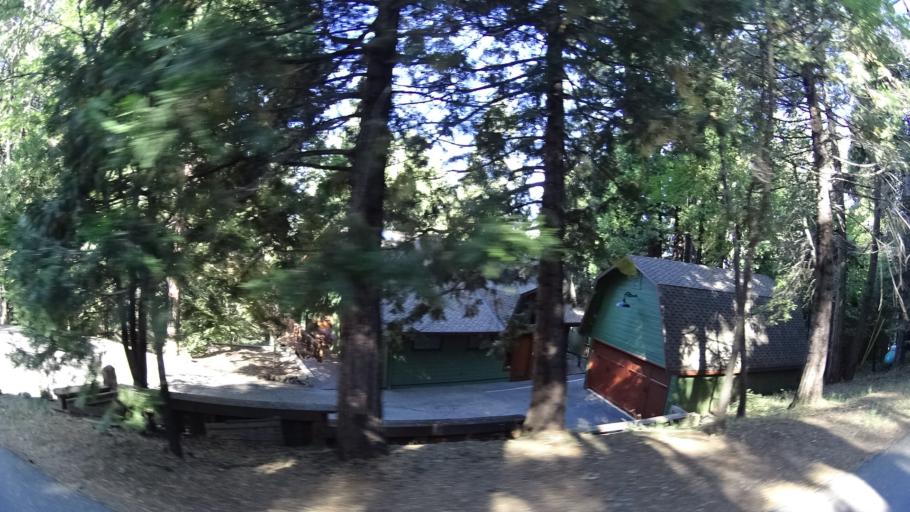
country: US
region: California
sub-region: Calaveras County
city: Arnold
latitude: 38.2604
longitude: -120.3188
